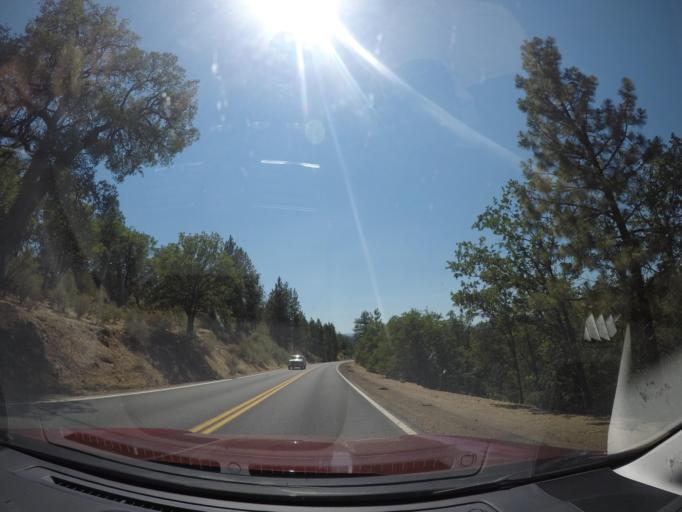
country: US
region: California
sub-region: Shasta County
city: Burney
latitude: 40.9847
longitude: -121.5189
